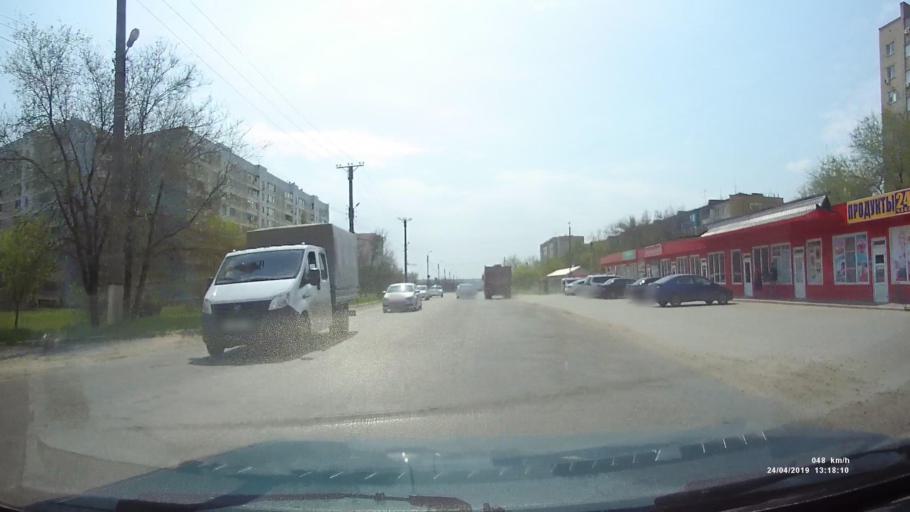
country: RU
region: Kalmykiya
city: Elista
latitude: 46.3035
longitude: 44.2958
